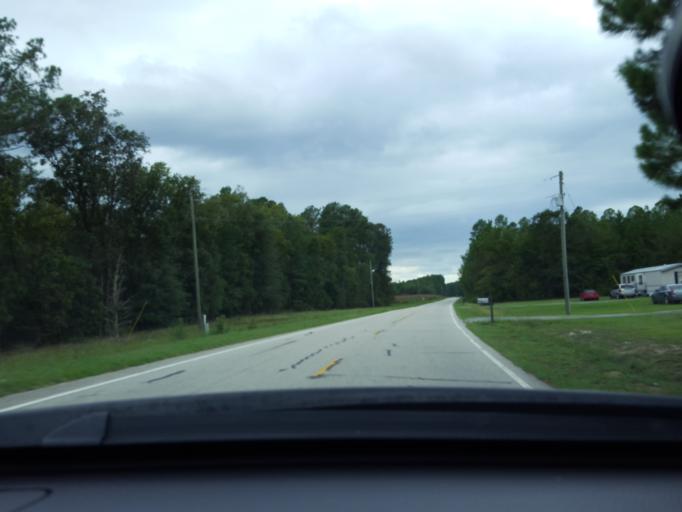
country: US
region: North Carolina
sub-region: Sampson County
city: Clinton
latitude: 34.7991
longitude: -78.2711
